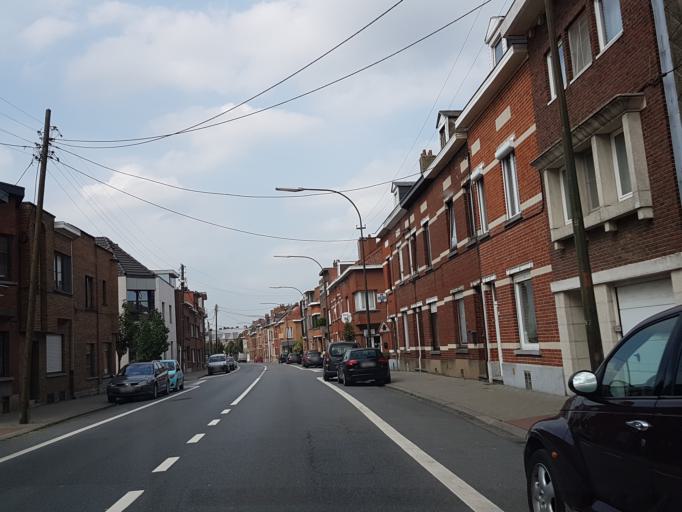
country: BE
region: Flanders
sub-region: Provincie Vlaams-Brabant
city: Zaventem
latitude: 50.8867
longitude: 4.4740
